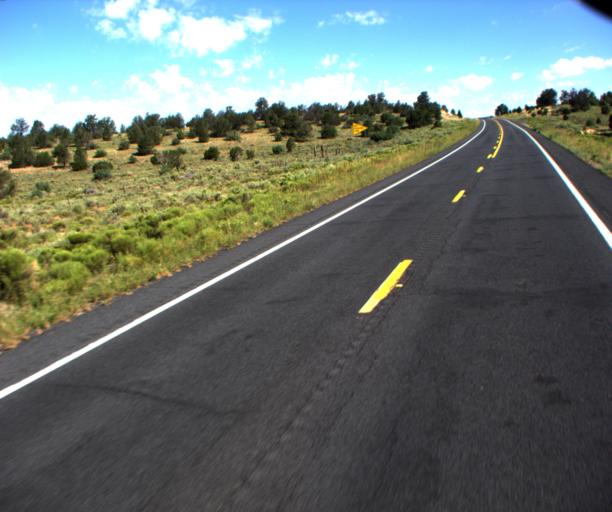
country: US
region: Arizona
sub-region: Coconino County
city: Grand Canyon Village
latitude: 35.7762
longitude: -112.1293
